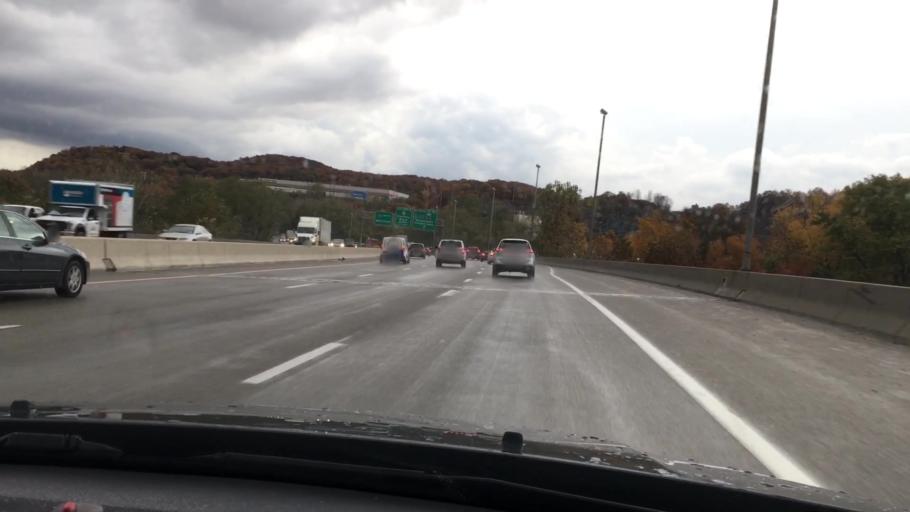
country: US
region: New Jersey
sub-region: Morris County
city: Riverdale
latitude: 40.9995
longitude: -74.3067
